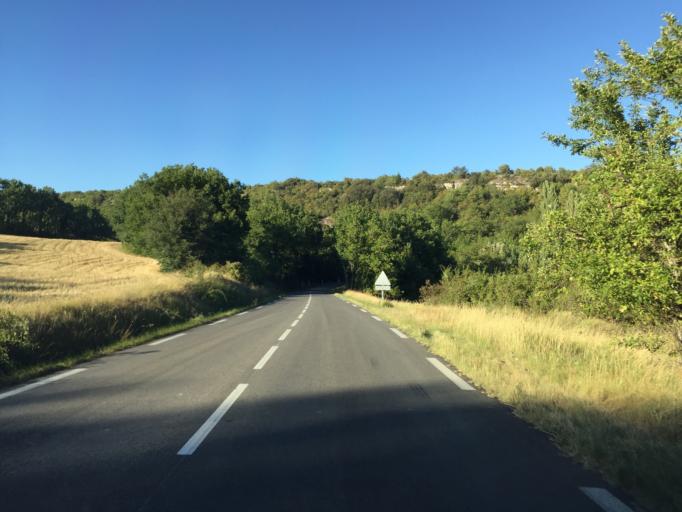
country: FR
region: Provence-Alpes-Cote d'Azur
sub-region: Departement des Alpes-de-Haute-Provence
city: Reillanne
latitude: 43.8894
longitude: 5.7205
